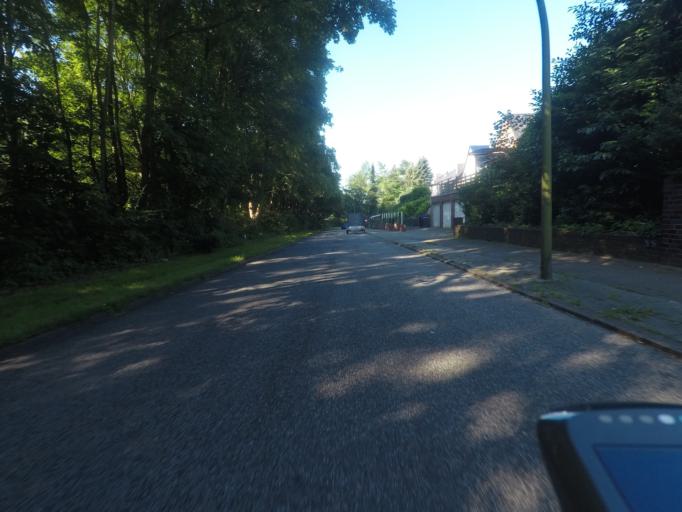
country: DE
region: Schleswig-Holstein
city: Oststeinbek
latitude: 53.5329
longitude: 10.1332
